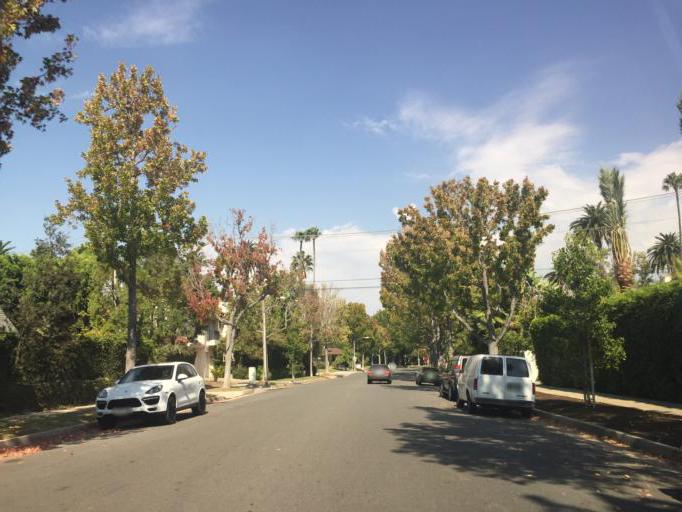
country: US
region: California
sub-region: Los Angeles County
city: Beverly Hills
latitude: 34.0804
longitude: -118.3972
